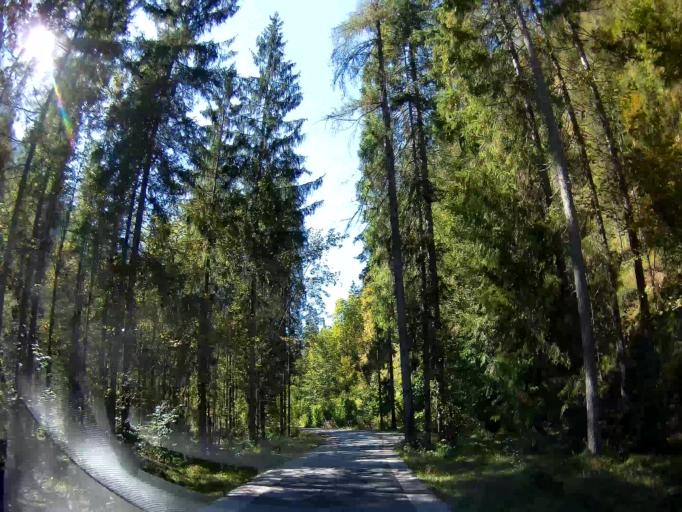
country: AT
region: Salzburg
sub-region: Politischer Bezirk Zell am See
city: Sankt Martin bei Lofer
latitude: 47.5288
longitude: 12.7156
